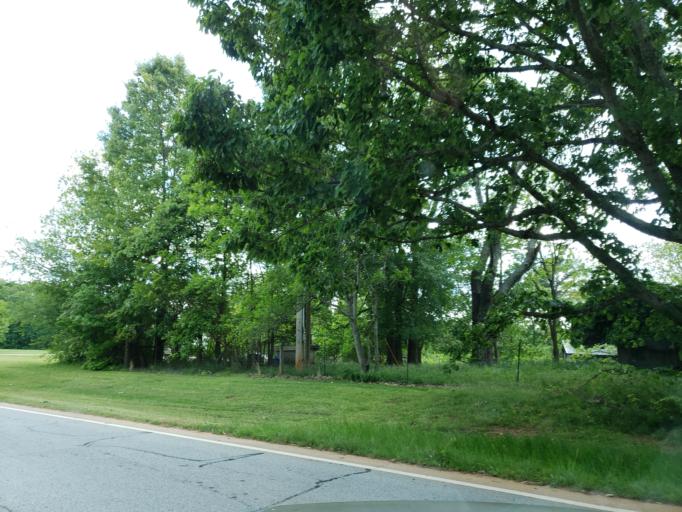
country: US
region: Georgia
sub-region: Haralson County
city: Tallapoosa
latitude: 33.6717
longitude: -85.2634
